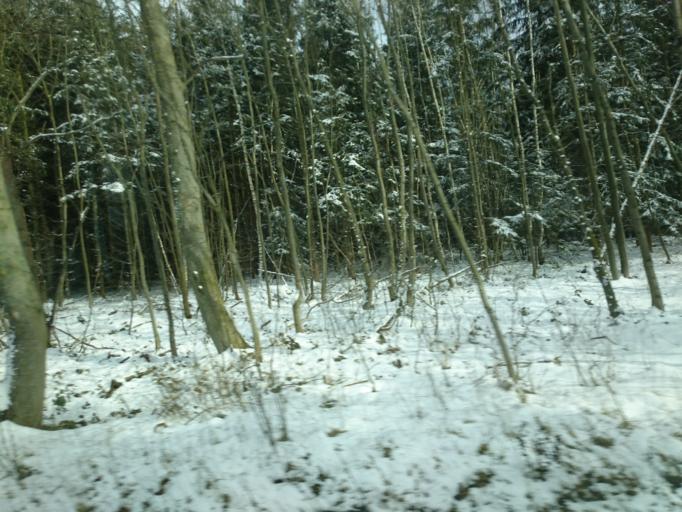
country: DE
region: Thuringia
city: Kospoda
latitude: 50.6952
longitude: 11.7697
